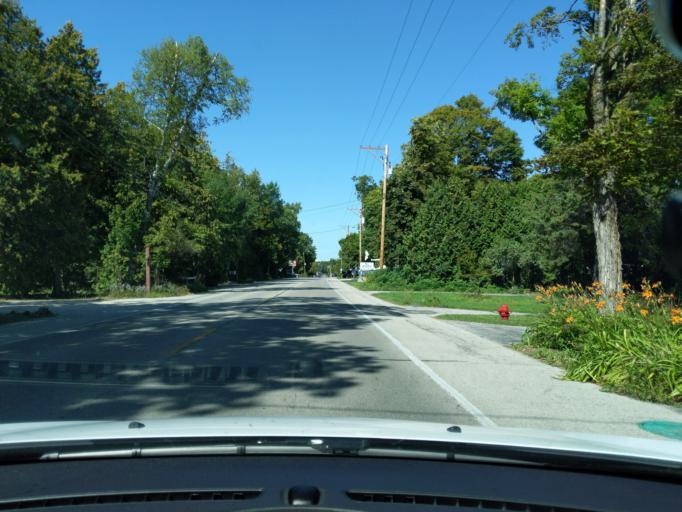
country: US
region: Wisconsin
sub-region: Door County
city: Sturgeon Bay
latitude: 45.1987
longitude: -87.1189
